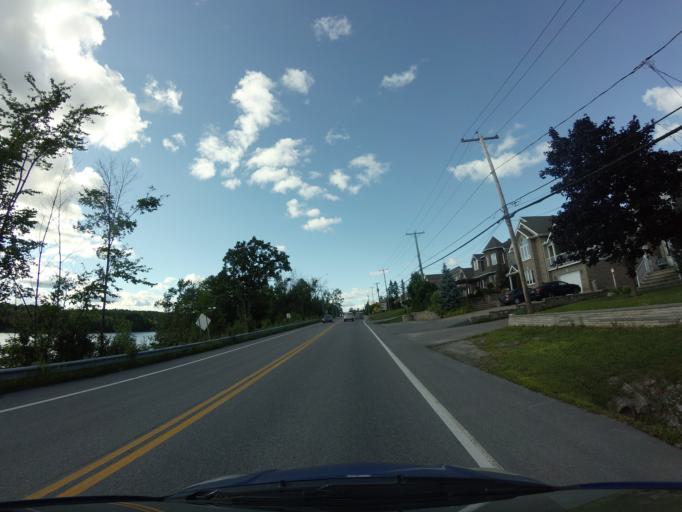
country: CA
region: Quebec
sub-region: Outaouais
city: Gatineau
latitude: 45.4819
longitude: -75.7404
